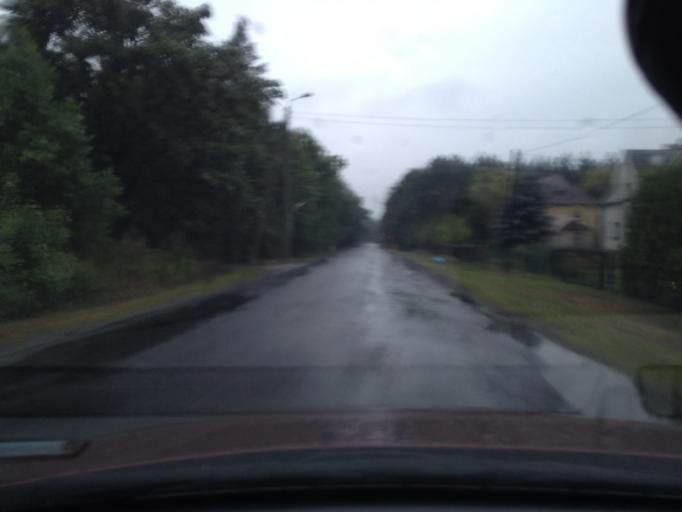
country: PL
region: Lubusz
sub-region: Powiat zaganski
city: Gozdnica
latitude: 51.3602
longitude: 15.1595
